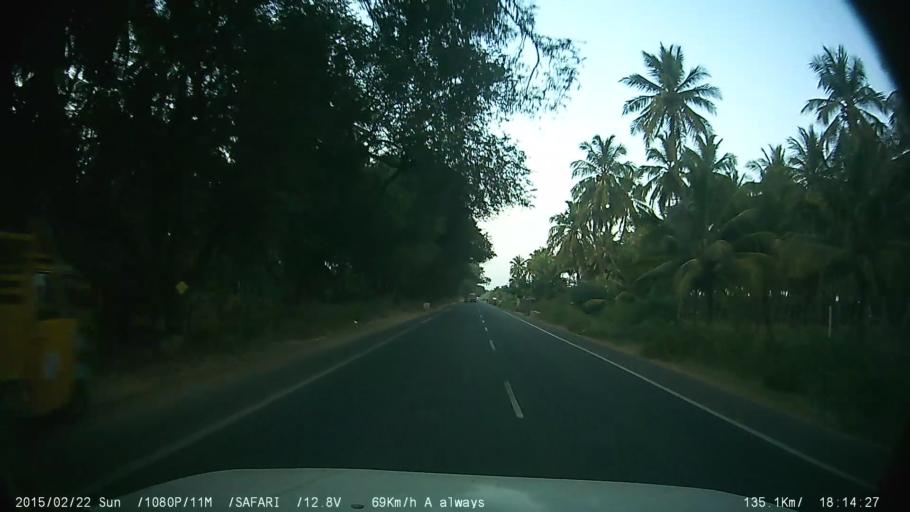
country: IN
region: Tamil Nadu
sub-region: Theni
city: Chinnamanur
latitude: 9.8584
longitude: 77.3882
